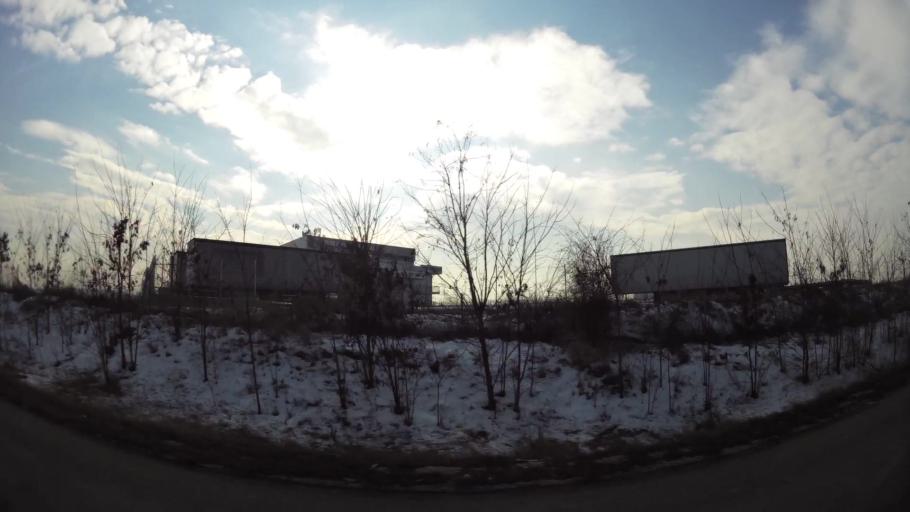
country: MK
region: Suto Orizari
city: Suto Orizare
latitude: 42.0501
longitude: 21.4310
